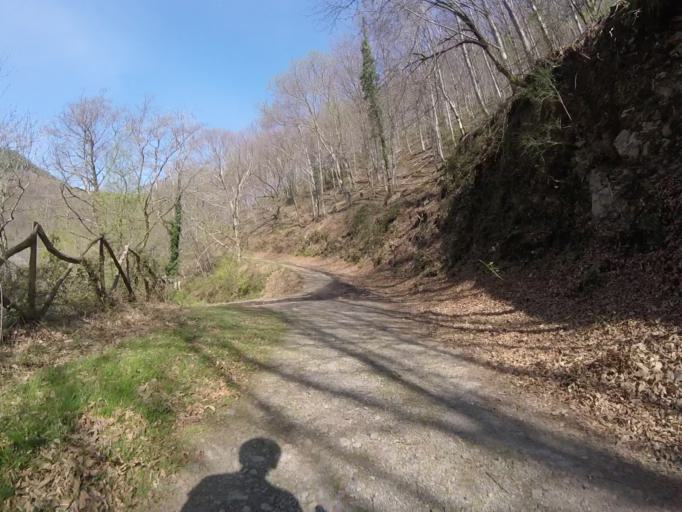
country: ES
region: Basque Country
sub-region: Provincia de Guipuzcoa
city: Irun
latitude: 43.2610
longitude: -1.8115
